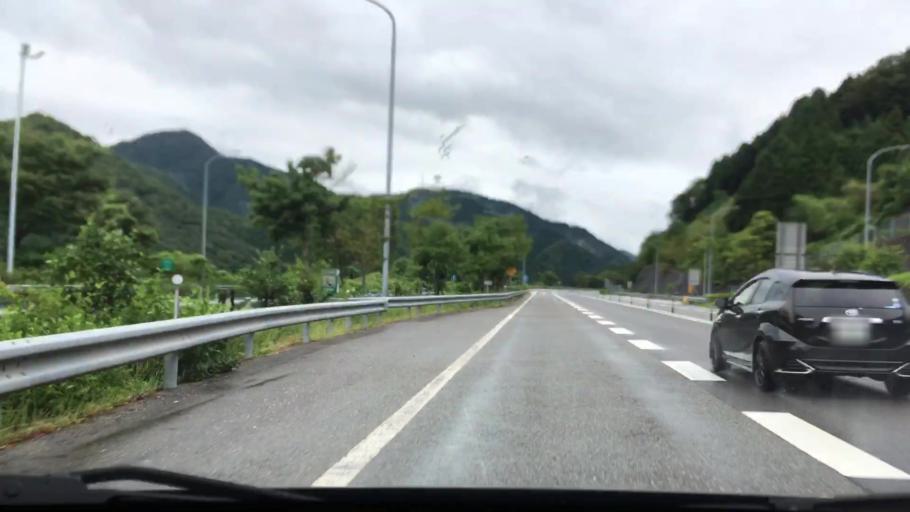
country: JP
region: Hyogo
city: Nishiwaki
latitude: 35.2125
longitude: 134.7941
